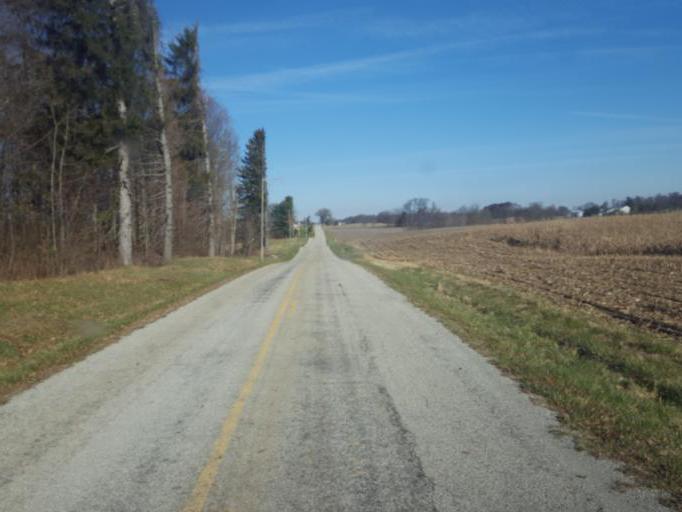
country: US
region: Ohio
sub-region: Crawford County
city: Crestline
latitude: 40.8634
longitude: -82.8274
